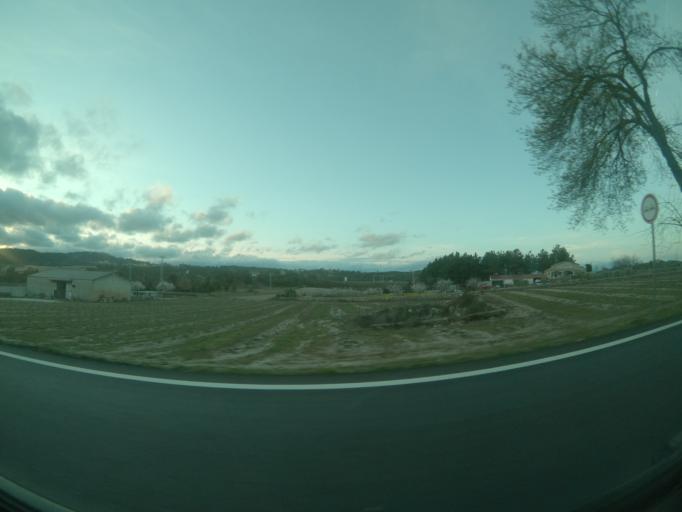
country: PT
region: Braganca
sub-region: Carrazeda de Ansiaes
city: Carrazeda de Anciaes
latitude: 41.2552
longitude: -7.2786
